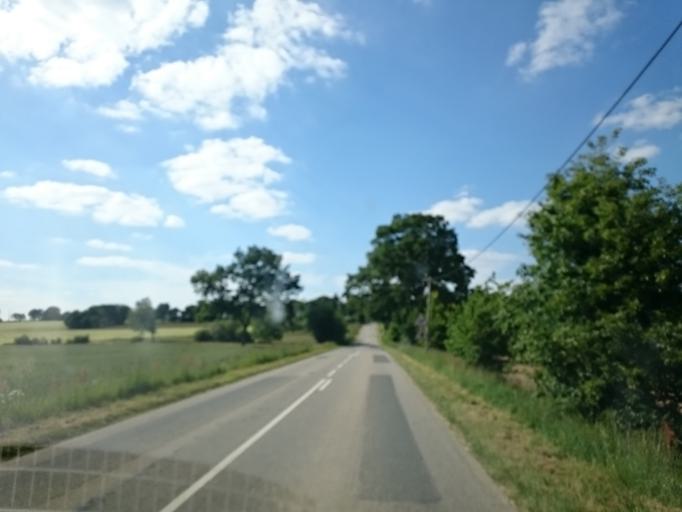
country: FR
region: Brittany
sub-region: Departement d'Ille-et-Vilaine
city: Chanteloup
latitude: 47.9466
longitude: -1.6093
